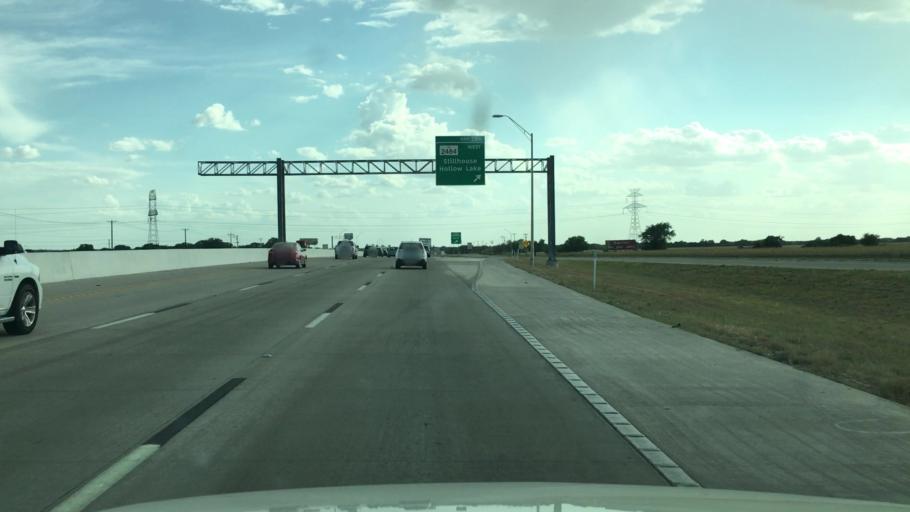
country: US
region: Texas
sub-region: Bell County
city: Salado
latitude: 30.9763
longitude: -97.5139
